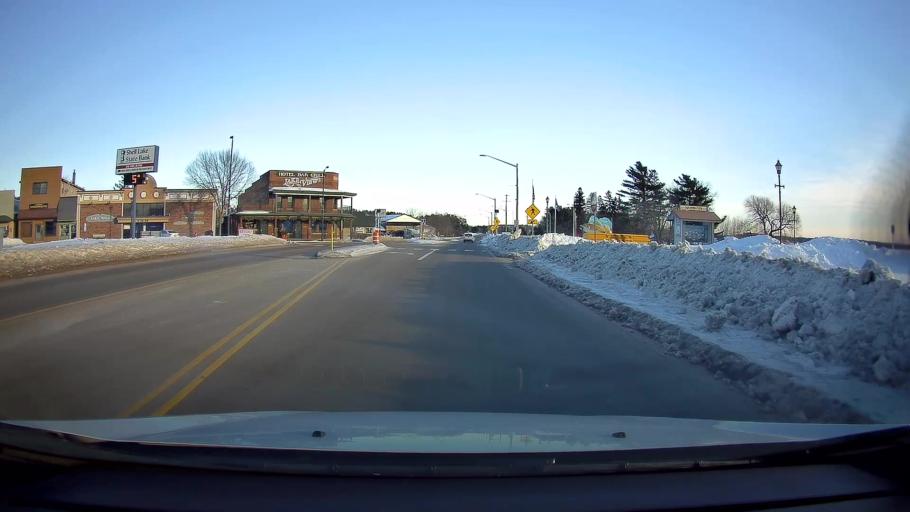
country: US
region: Wisconsin
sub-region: Washburn County
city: Shell Lake
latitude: 45.7426
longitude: -91.9239
